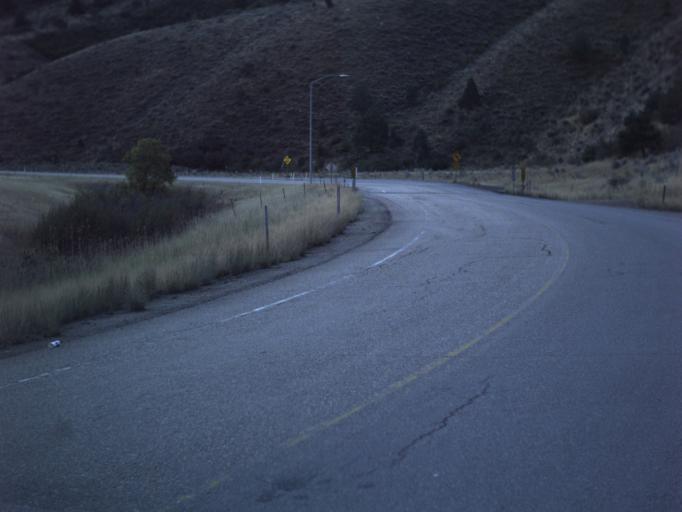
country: US
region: Utah
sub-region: Morgan County
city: Morgan
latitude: 41.0585
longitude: -111.5403
